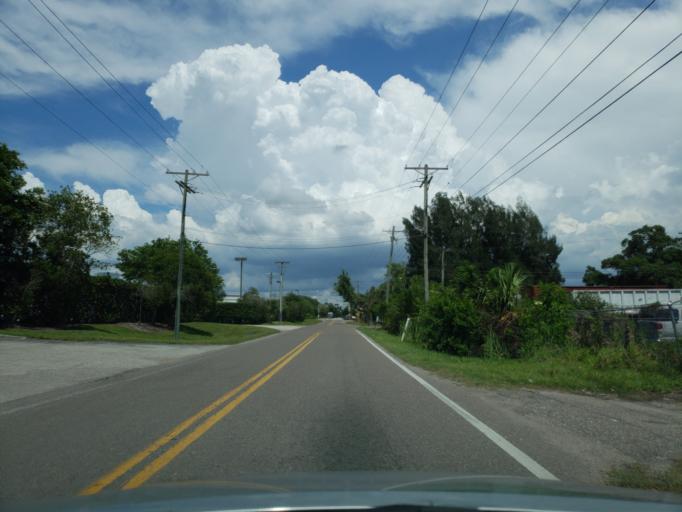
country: US
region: Florida
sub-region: Hillsborough County
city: Palm River-Clair Mel
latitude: 27.9336
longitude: -82.4000
